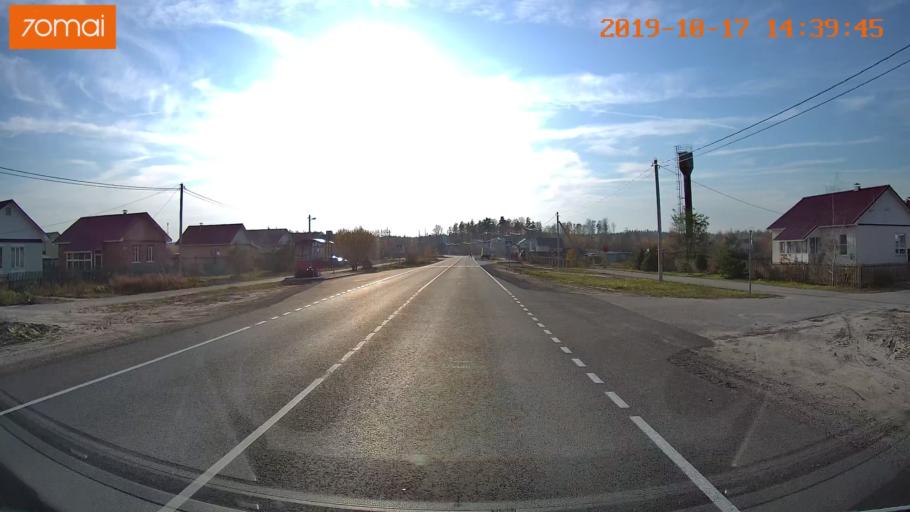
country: RU
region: Rjazan
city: Solotcha
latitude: 54.8601
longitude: 39.9653
